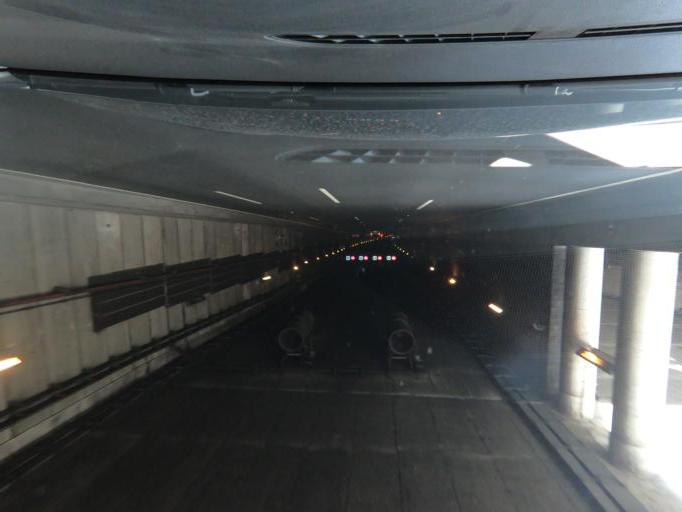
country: PT
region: Lisbon
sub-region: Odivelas
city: Pontinha
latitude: 38.7468
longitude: -9.2088
